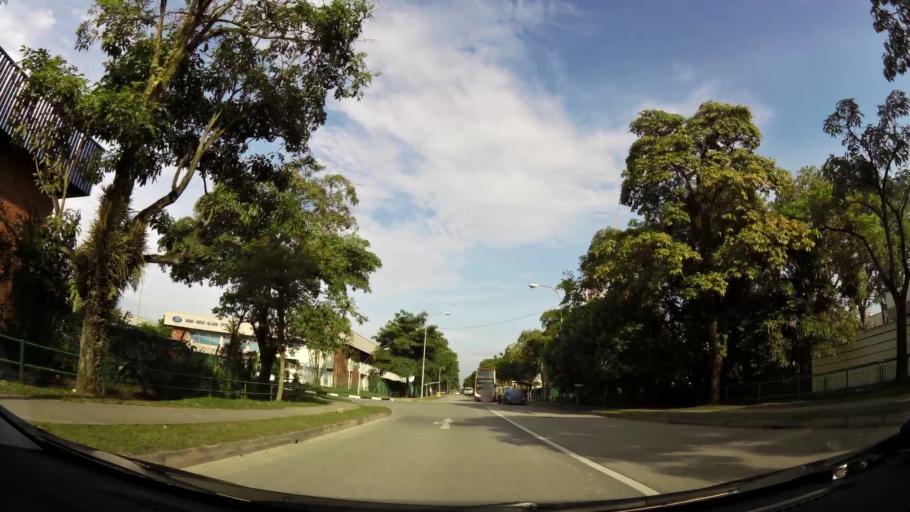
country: MY
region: Johor
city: Johor Bahru
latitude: 1.3234
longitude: 103.6592
